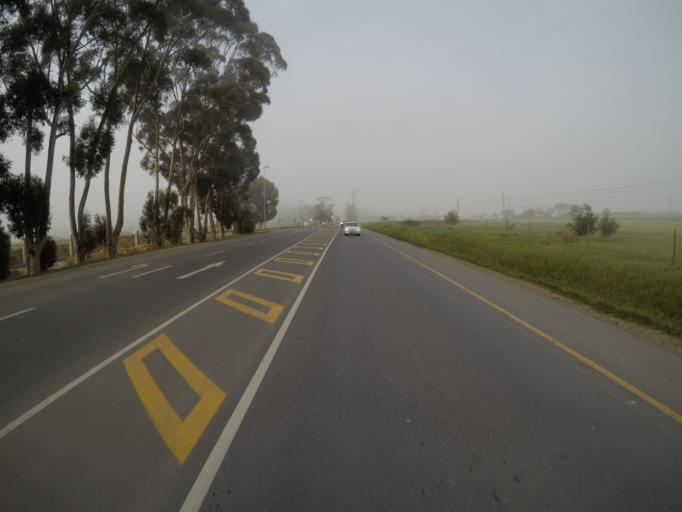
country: ZA
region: Western Cape
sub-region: City of Cape Town
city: Kraaifontein
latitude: -33.7911
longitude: 18.6974
